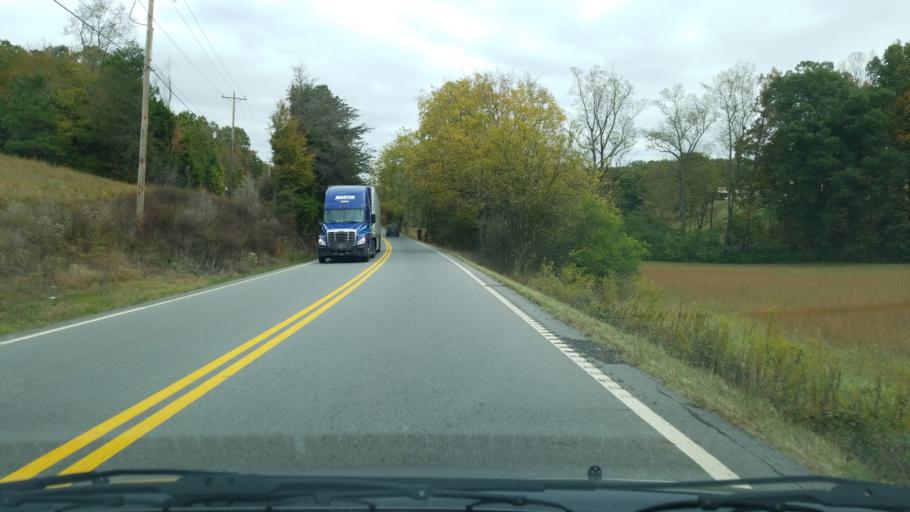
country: US
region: Tennessee
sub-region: Hamilton County
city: Sale Creek
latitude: 35.3500
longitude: -84.9867
